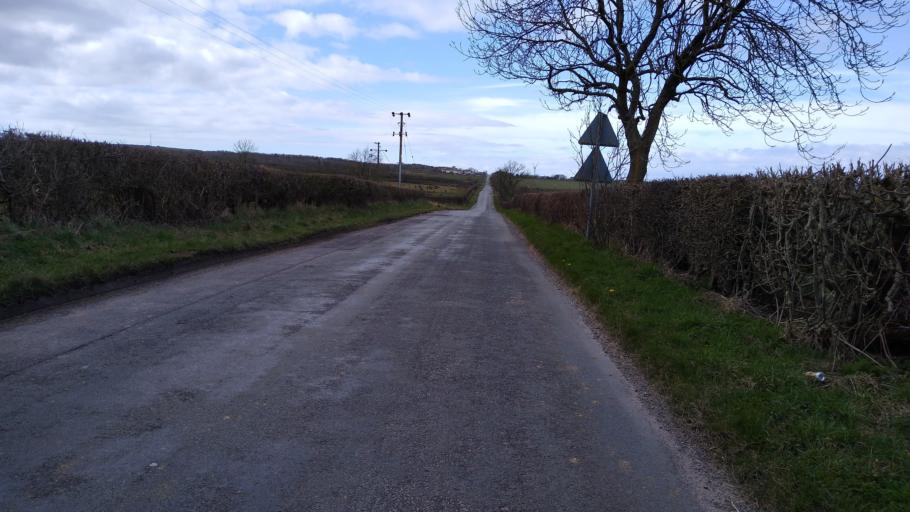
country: GB
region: England
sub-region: Cumbria
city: Dearham
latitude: 54.6916
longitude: -3.4486
